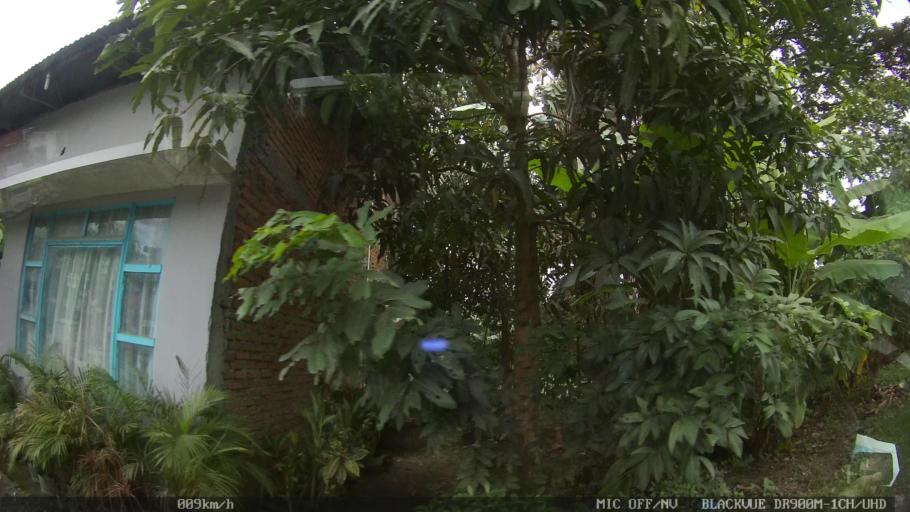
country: ID
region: North Sumatra
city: Sunggal
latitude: 3.6352
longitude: 98.5913
